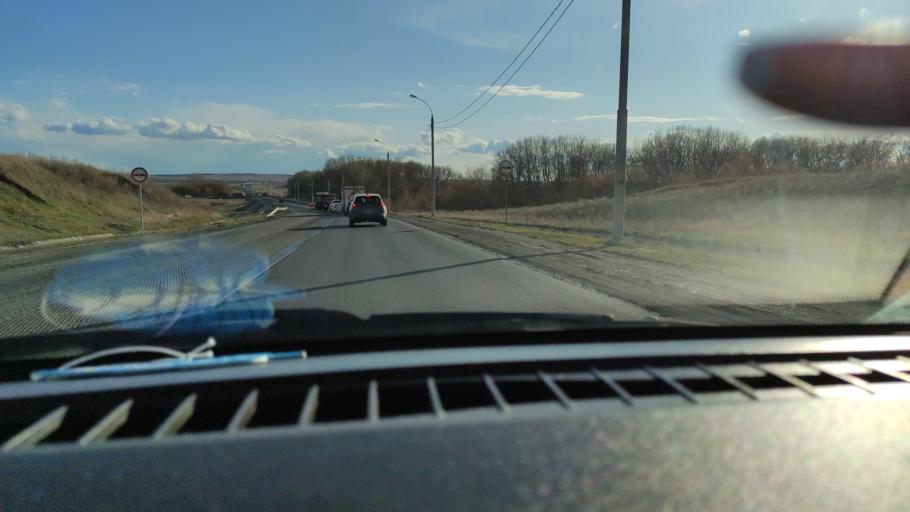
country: RU
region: Saratov
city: Yelshanka
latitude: 51.8263
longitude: 46.2221
